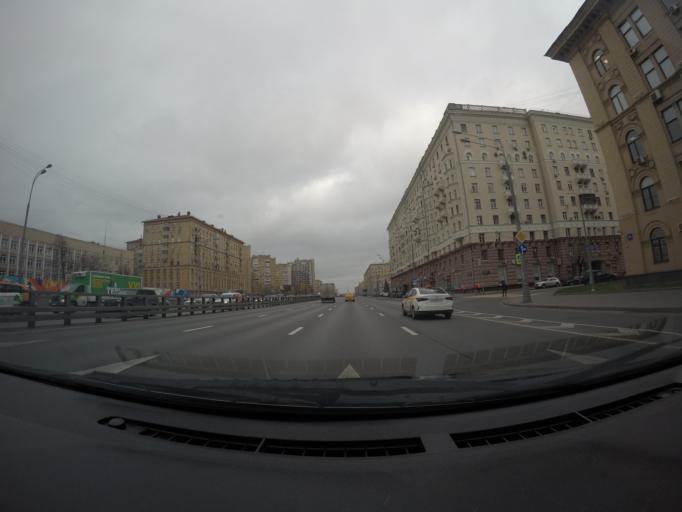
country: RU
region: Moscow
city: Mar'ina Roshcha
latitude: 55.8031
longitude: 37.6363
